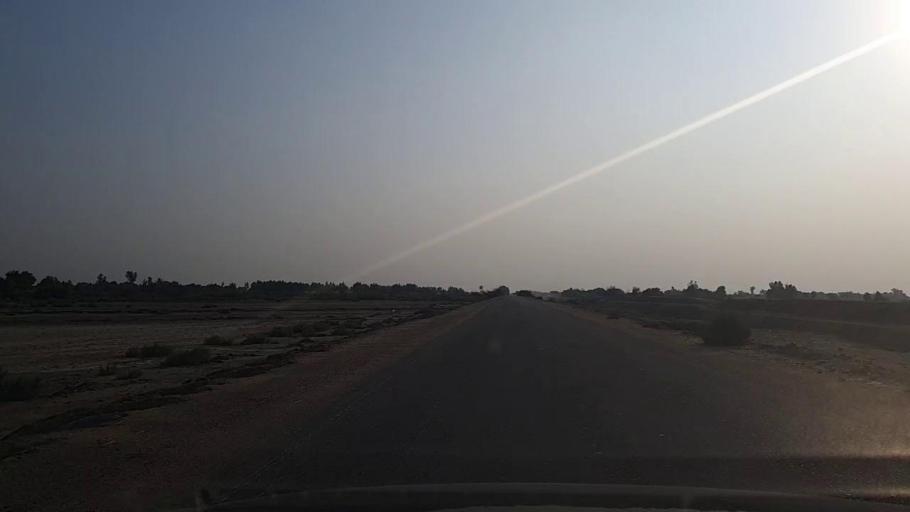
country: PK
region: Sindh
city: Mirpur Sakro
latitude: 24.5061
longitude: 67.8165
